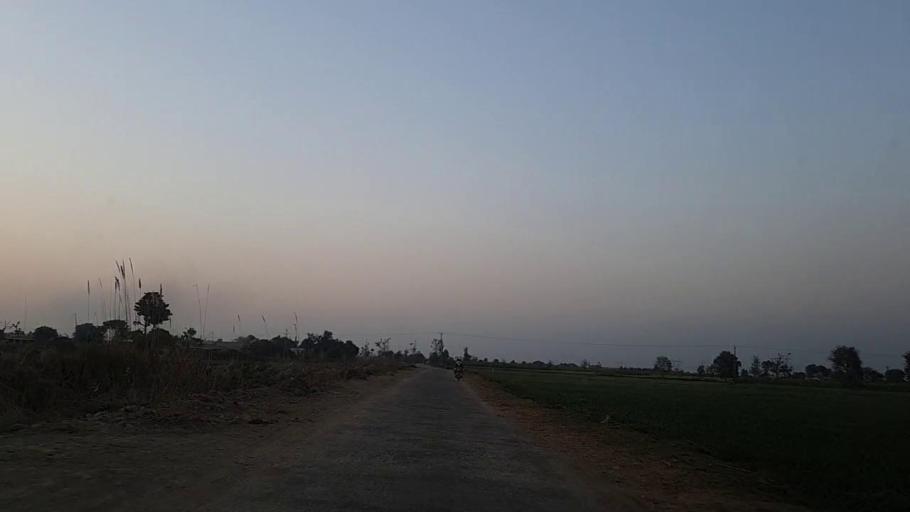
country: PK
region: Sindh
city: Hala
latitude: 25.9536
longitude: 68.4250
